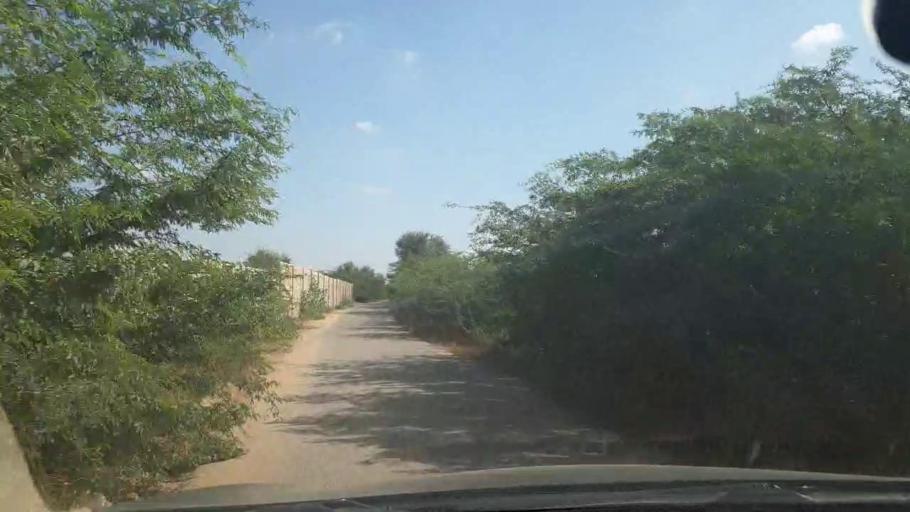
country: PK
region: Sindh
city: Malir Cantonment
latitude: 25.0586
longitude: 67.3918
